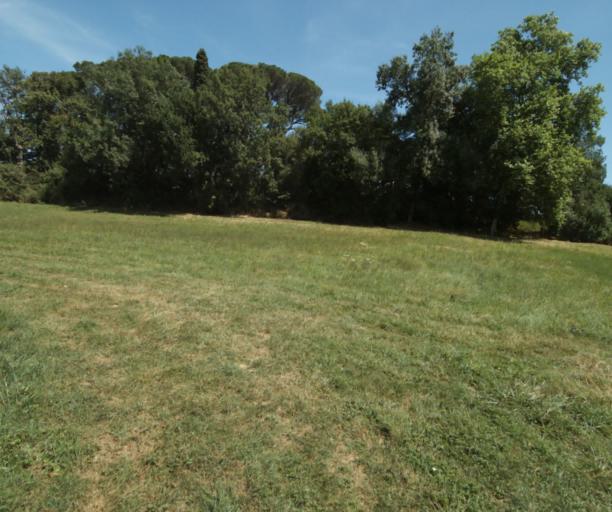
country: FR
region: Midi-Pyrenees
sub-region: Departement de la Haute-Garonne
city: Revel
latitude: 43.4991
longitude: 2.0194
